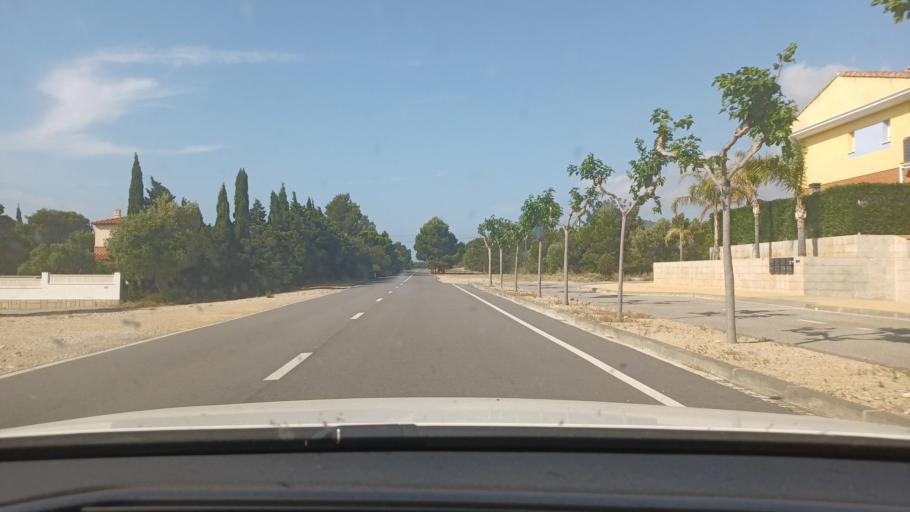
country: ES
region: Catalonia
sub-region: Provincia de Tarragona
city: Colldejou
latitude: 40.9852
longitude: 0.9077
